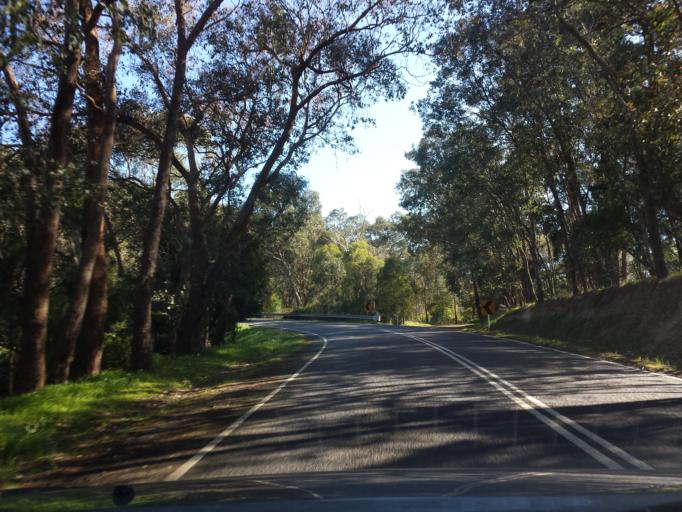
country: AU
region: Victoria
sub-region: Yarra Ranges
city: Yarra Glen
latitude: -37.6472
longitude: 145.3571
